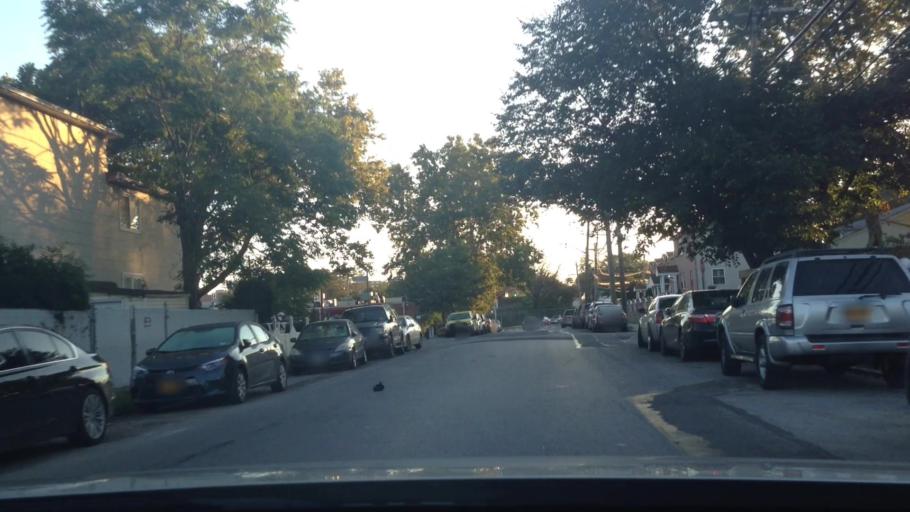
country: US
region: New York
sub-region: Queens County
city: Jamaica
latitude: 40.6701
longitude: -73.7751
